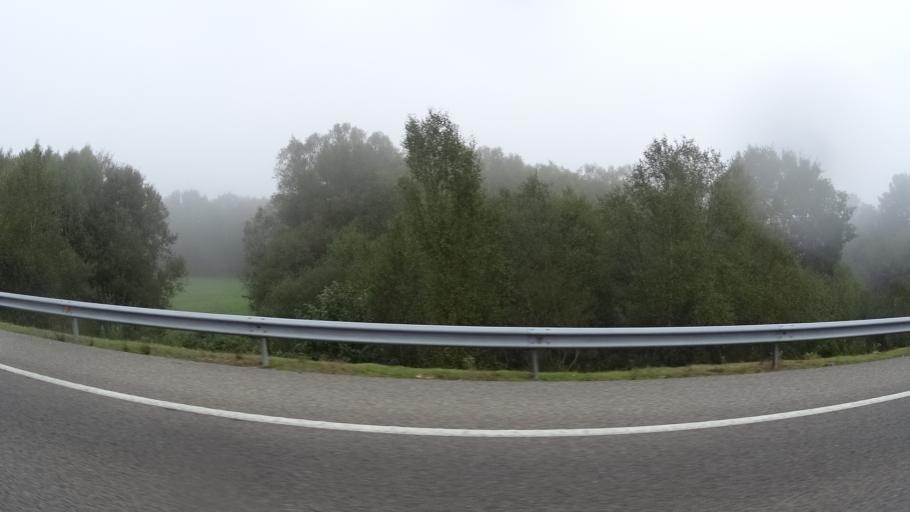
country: ES
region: Galicia
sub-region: Provincia de Lugo
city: Guitiriz
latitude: 43.1879
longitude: -7.8472
